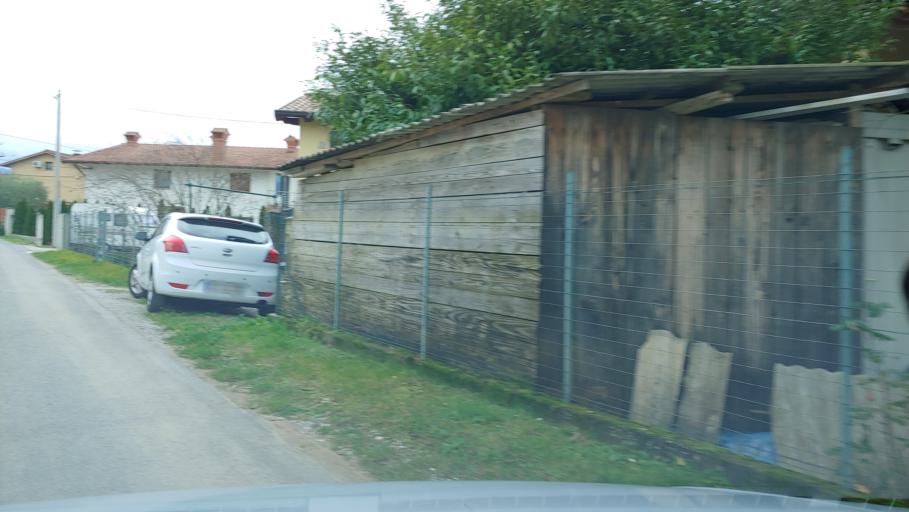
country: SI
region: Miren-Kostanjevica
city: Miren
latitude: 45.8870
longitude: 13.6097
